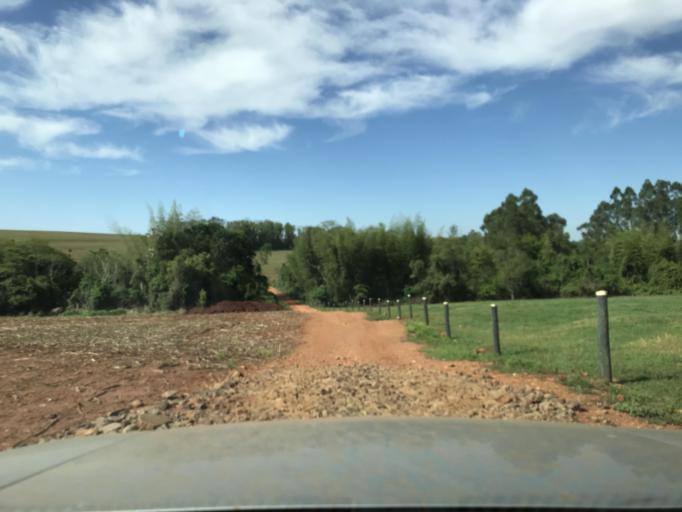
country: BR
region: Parana
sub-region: Palotina
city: Palotina
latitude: -24.1803
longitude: -53.8391
